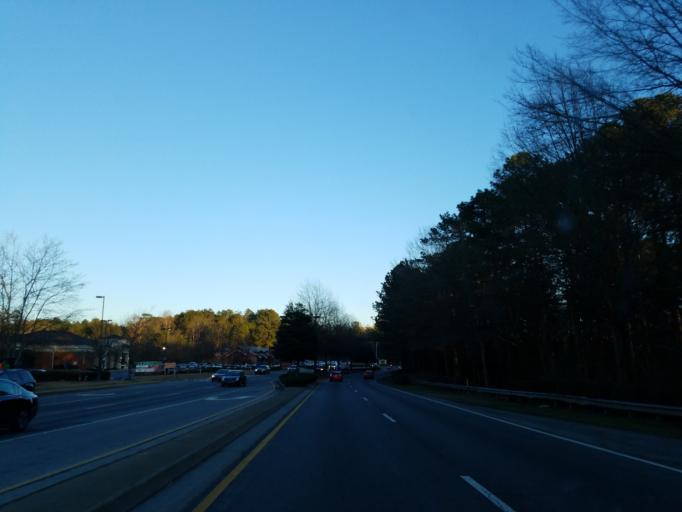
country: US
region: Georgia
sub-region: Cherokee County
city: Woodstock
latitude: 34.1047
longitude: -84.5417
